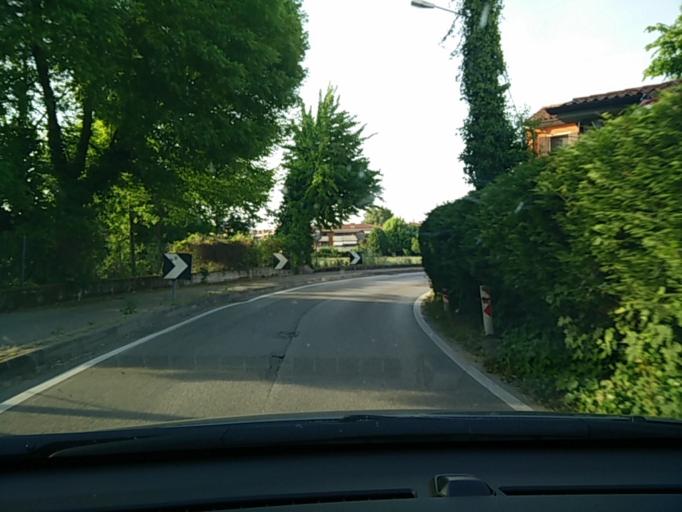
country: IT
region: Veneto
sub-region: Provincia di Padova
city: Sarmeola
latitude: 45.4251
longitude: 11.8397
